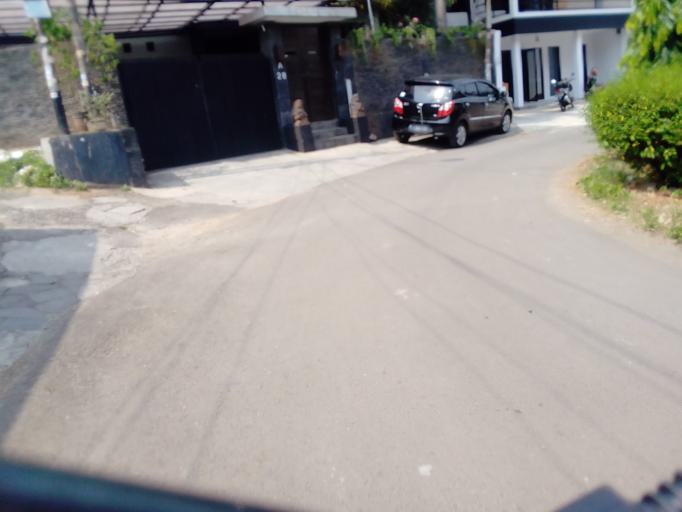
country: ID
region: Jakarta Raya
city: Jakarta
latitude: -6.2066
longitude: 106.8094
